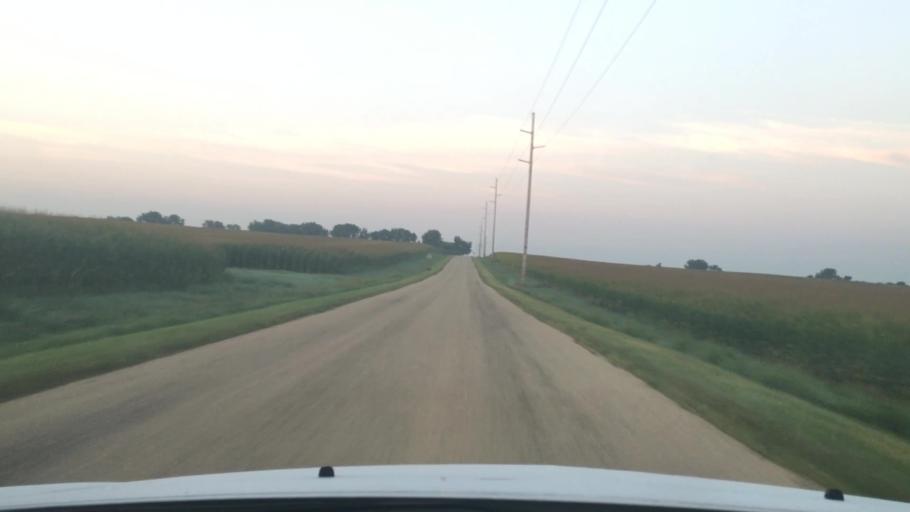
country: US
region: Illinois
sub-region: Ogle County
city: Rochelle
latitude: 41.8896
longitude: -89.0009
